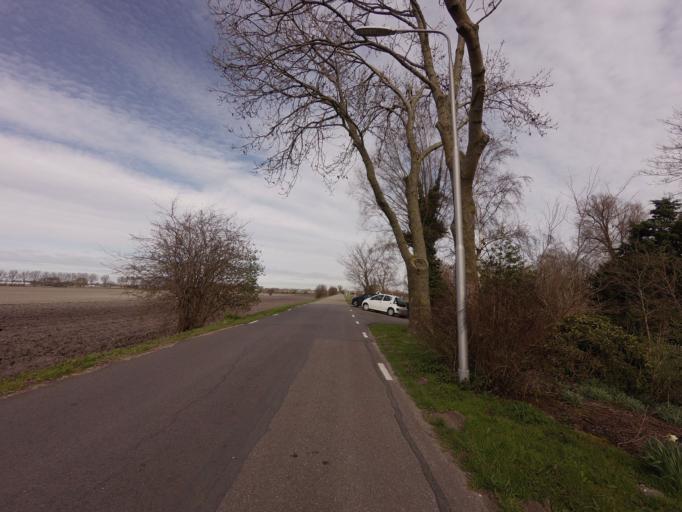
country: NL
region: North Holland
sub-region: Gemeente Uithoorn
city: Uithoorn
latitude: 52.2587
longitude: 4.8384
